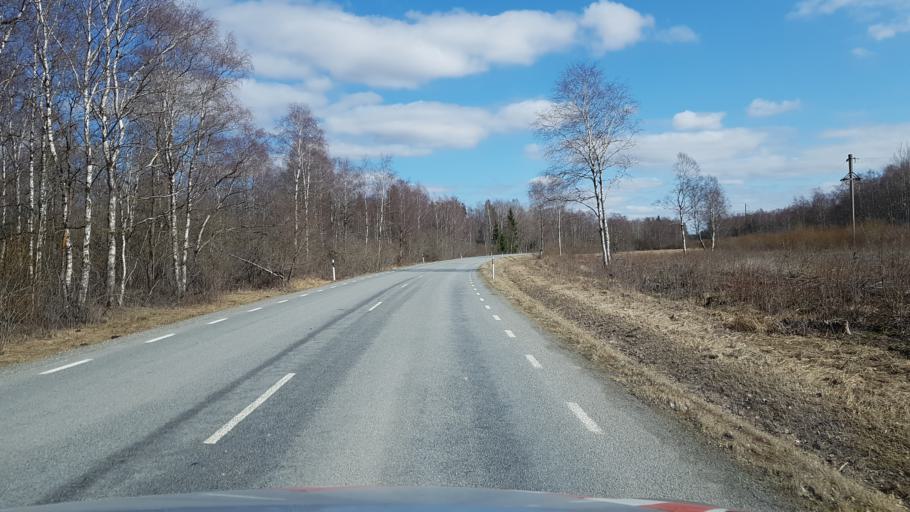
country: EE
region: Laeaene-Virumaa
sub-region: Tapa vald
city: Tapa
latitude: 59.2784
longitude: 25.8840
